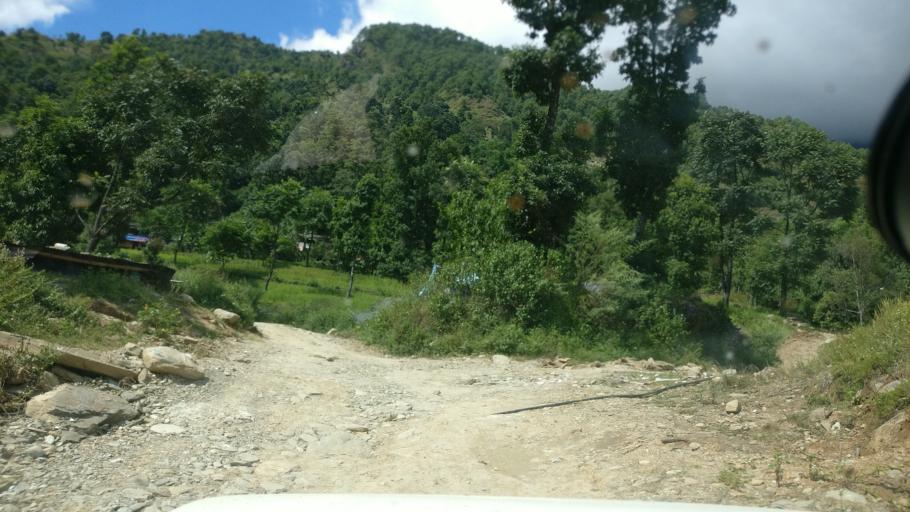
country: NP
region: Western Region
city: Baglung
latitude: 28.2599
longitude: 83.6544
